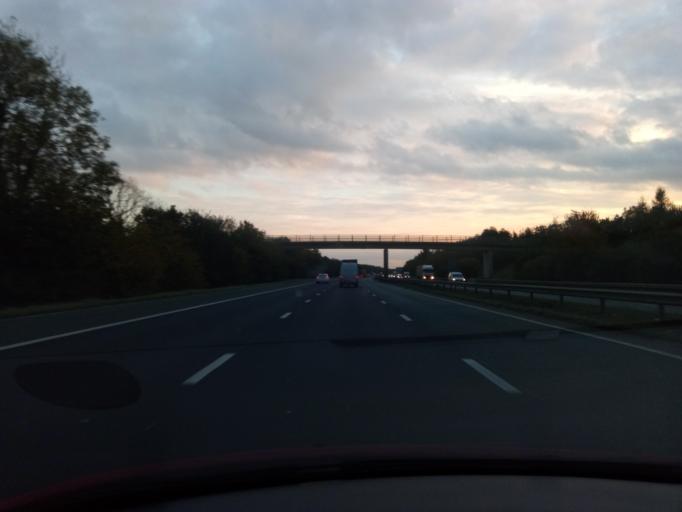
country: GB
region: England
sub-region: City and Borough of Leeds
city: Wetherby
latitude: 53.9929
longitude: -1.3637
